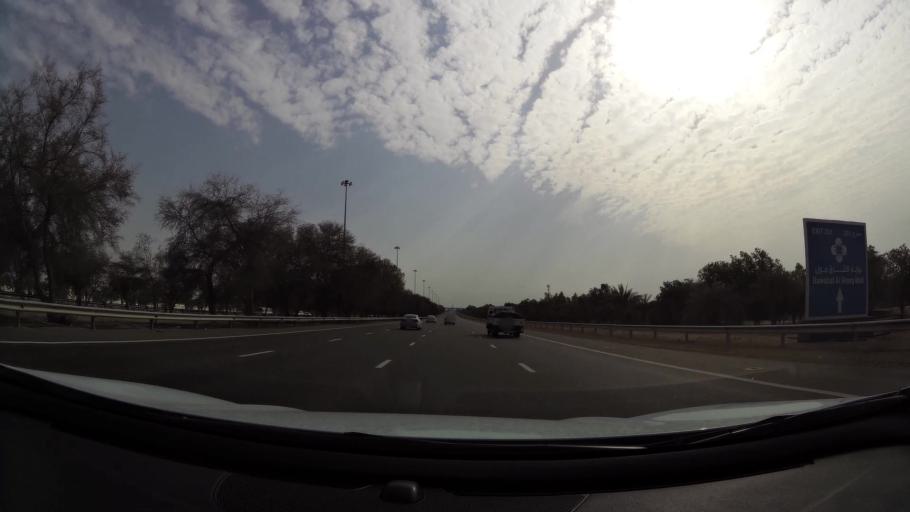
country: AE
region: Abu Dhabi
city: Abu Dhabi
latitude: 24.4975
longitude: 54.6801
